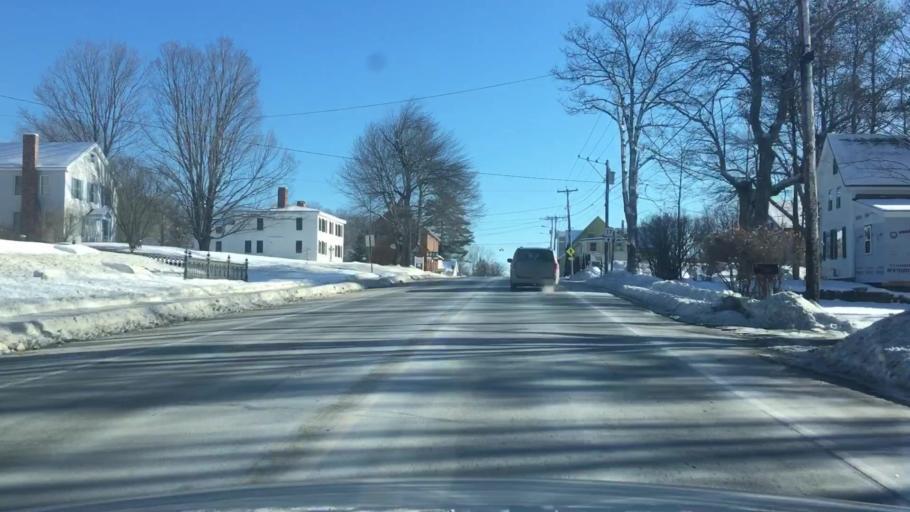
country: US
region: Maine
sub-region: Kennebec County
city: Readfield
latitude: 44.3880
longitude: -69.9687
